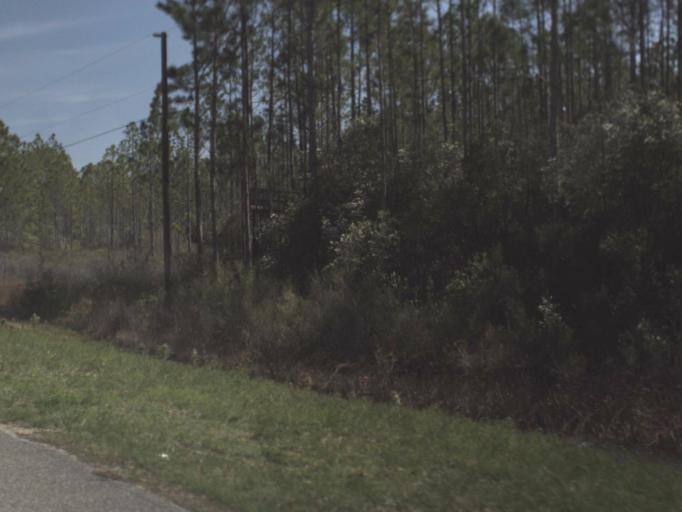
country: US
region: Florida
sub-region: Gulf County
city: Port Saint Joe
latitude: 29.7365
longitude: -85.1675
